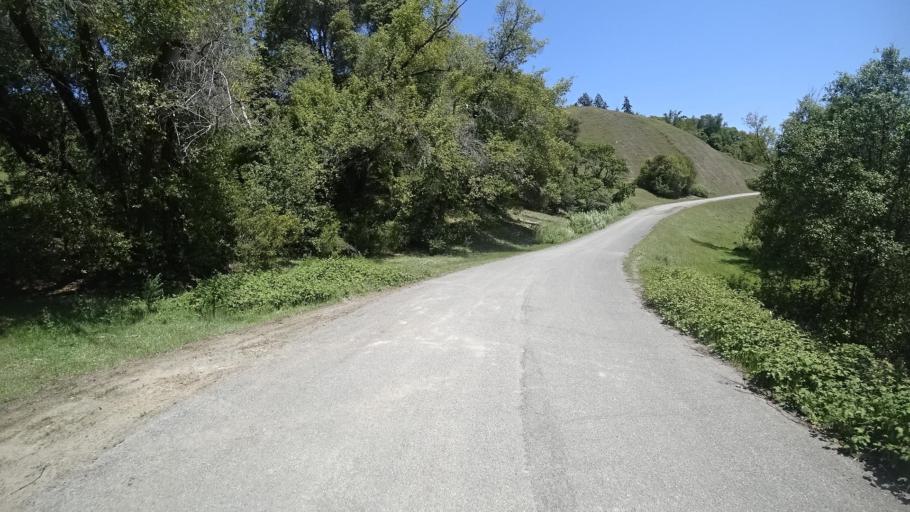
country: US
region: California
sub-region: Humboldt County
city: Redway
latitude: 40.1938
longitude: -123.5670
